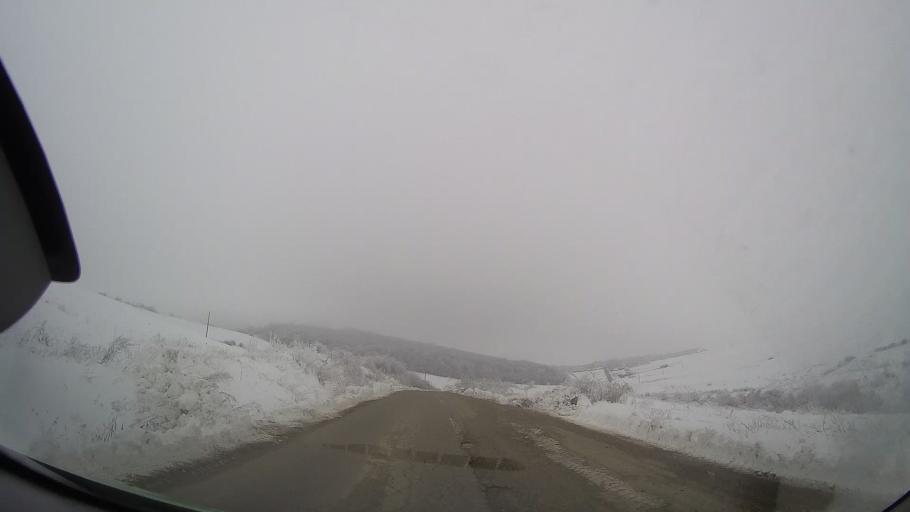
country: RO
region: Neamt
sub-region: Comuna Pancesti
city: Pancesti
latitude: 46.9180
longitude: 27.1630
